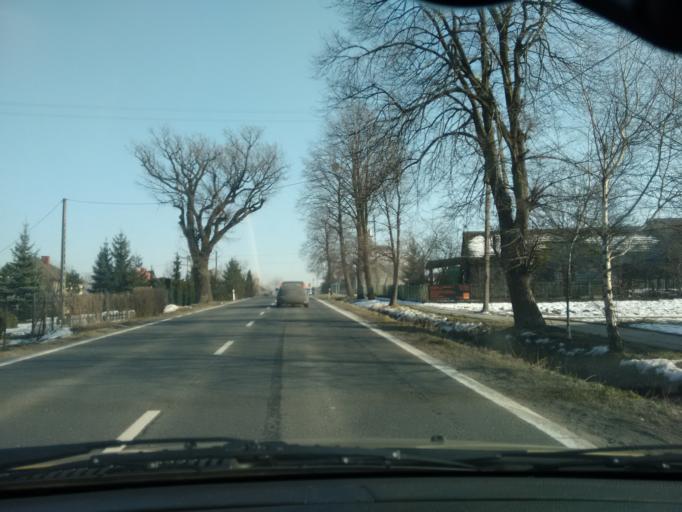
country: PL
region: Lesser Poland Voivodeship
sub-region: Powiat oswiecimski
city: Bulowice
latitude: 49.8786
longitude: 19.2698
